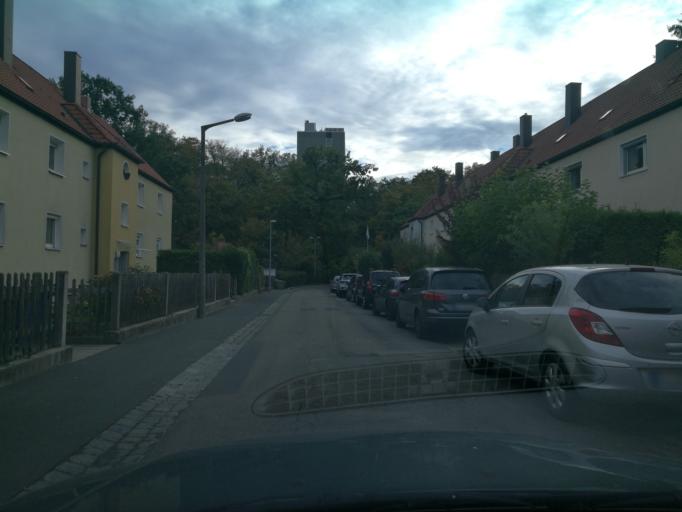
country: DE
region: Bavaria
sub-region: Regierungsbezirk Mittelfranken
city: Furth
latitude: 49.4867
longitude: 10.9771
